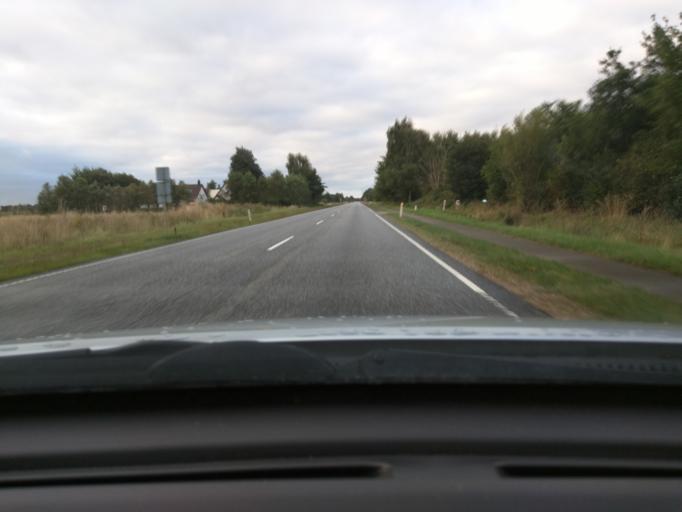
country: DK
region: Central Jutland
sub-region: Ikast-Brande Kommune
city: Bording Kirkeby
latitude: 56.2472
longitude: 9.3214
